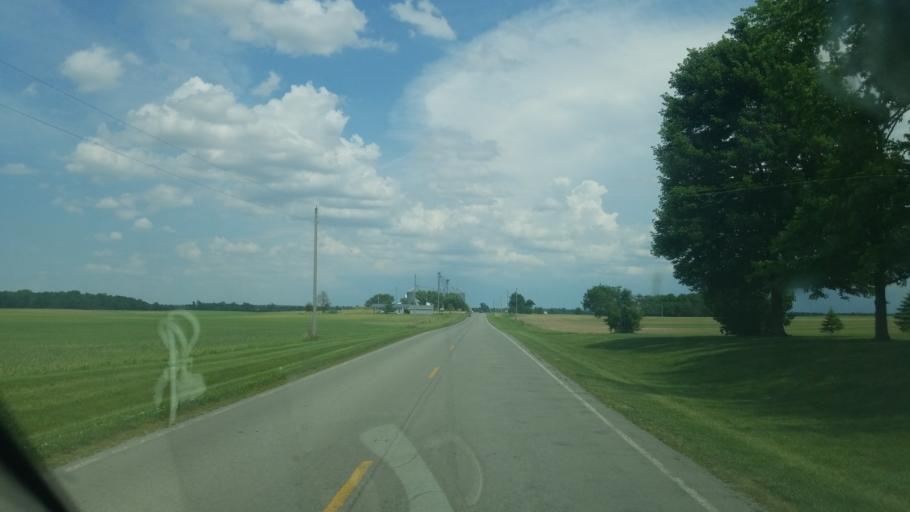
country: US
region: Ohio
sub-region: Hardin County
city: Ada
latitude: 40.6159
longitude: -83.8299
